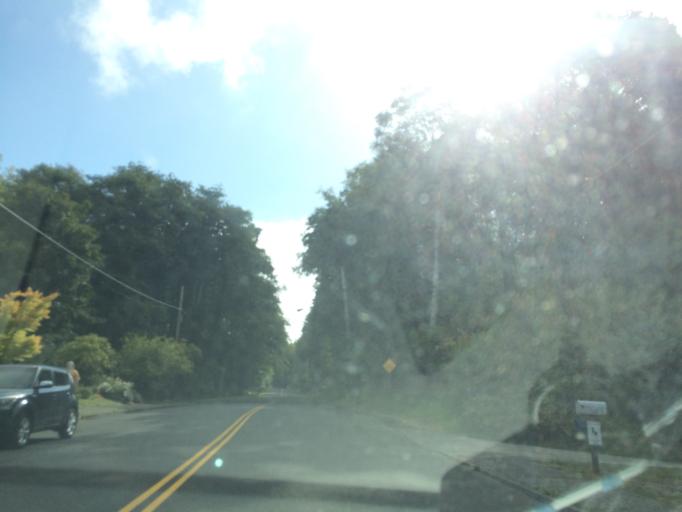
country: US
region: Oregon
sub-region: Clatsop County
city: Astoria
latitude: 46.1855
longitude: -123.8192
